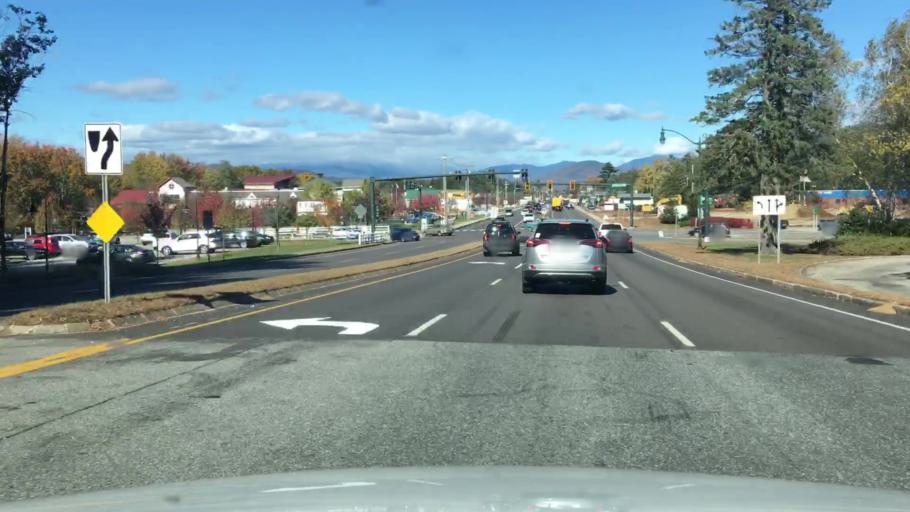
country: US
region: New Hampshire
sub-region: Carroll County
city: Conway
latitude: 44.0166
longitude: -71.1142
